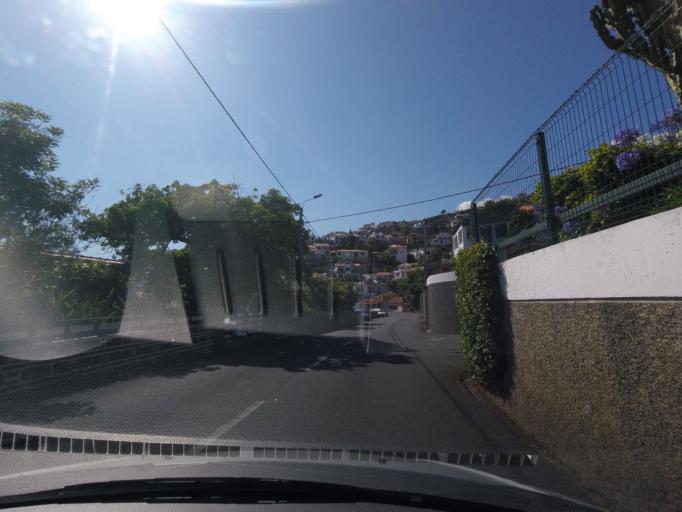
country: PT
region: Madeira
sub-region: Funchal
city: Nossa Senhora do Monte
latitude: 32.6663
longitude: -16.9112
